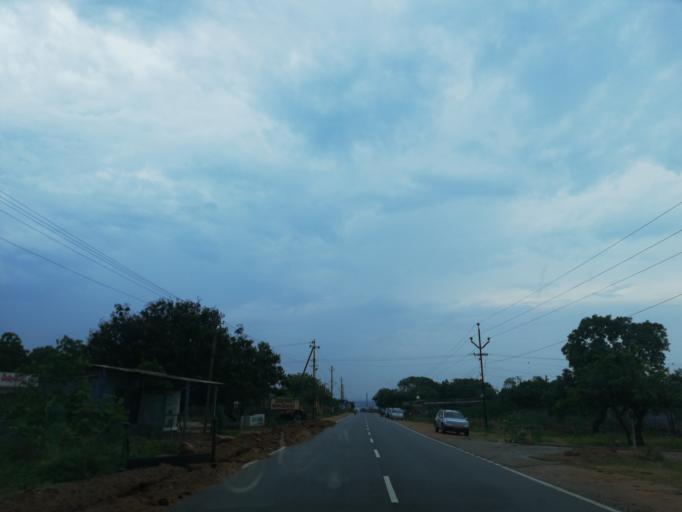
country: IN
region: Andhra Pradesh
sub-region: Guntur
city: Macherla
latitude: 16.6139
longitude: 79.2971
